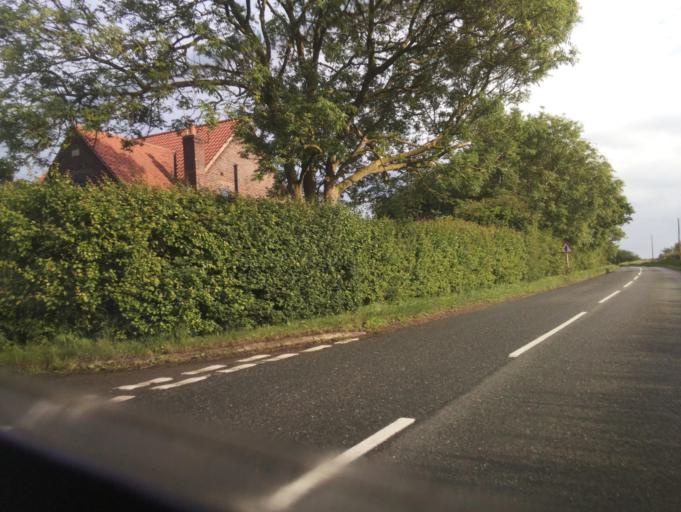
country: GB
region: England
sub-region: Lincolnshire
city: Great Gonerby
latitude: 53.0243
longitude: -0.6560
